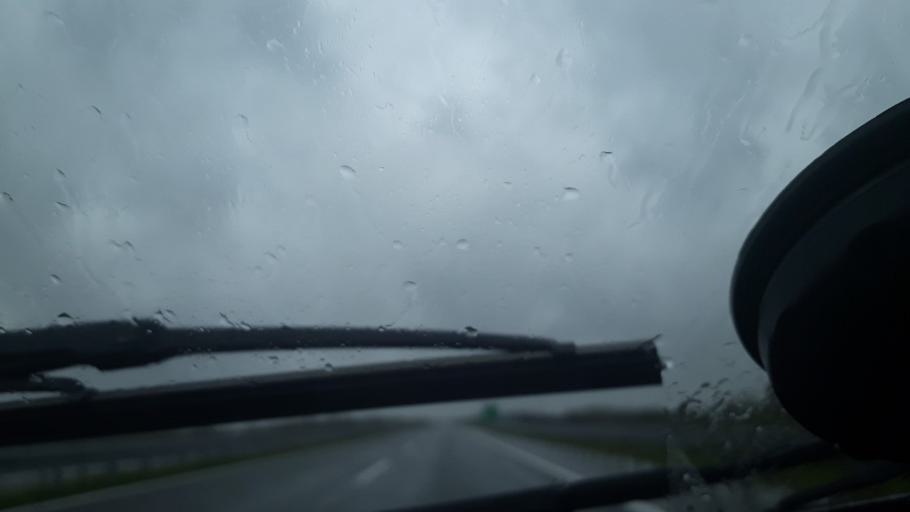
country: BA
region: Republika Srpska
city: Bosanska Gradiska
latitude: 45.0917
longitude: 17.1941
